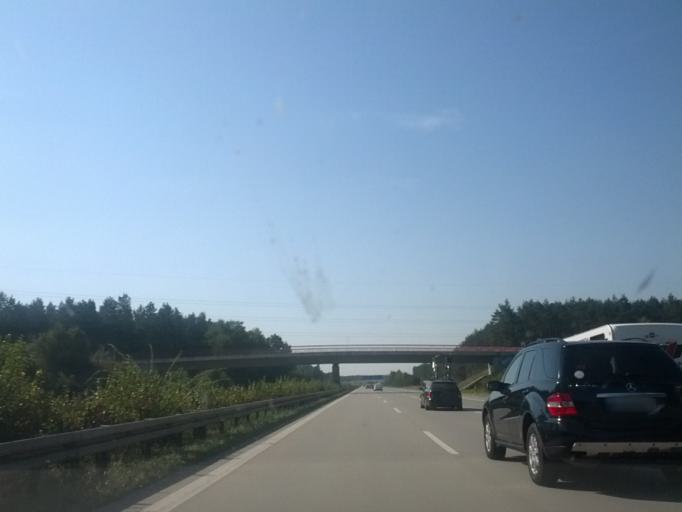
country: DE
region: Brandenburg
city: Erkner
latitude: 52.3377
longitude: 13.7532
